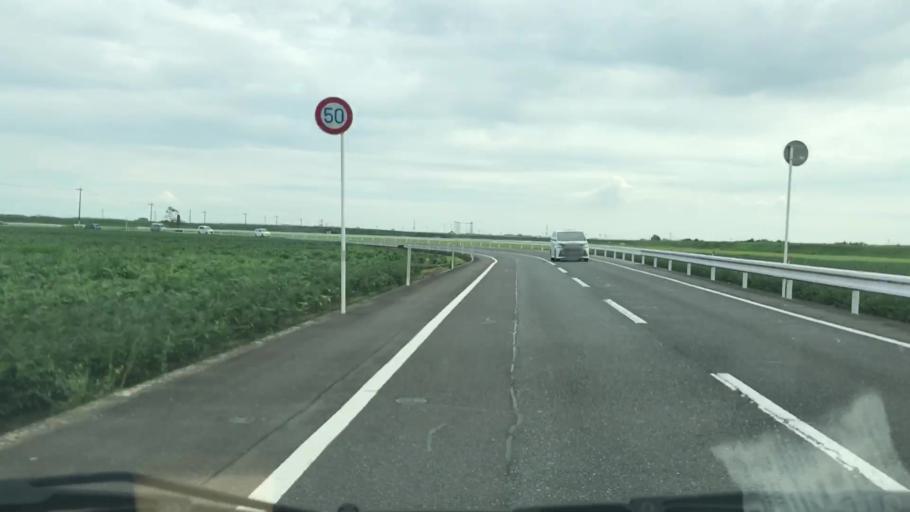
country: JP
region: Saga Prefecture
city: Saga-shi
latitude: 33.2900
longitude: 130.2401
